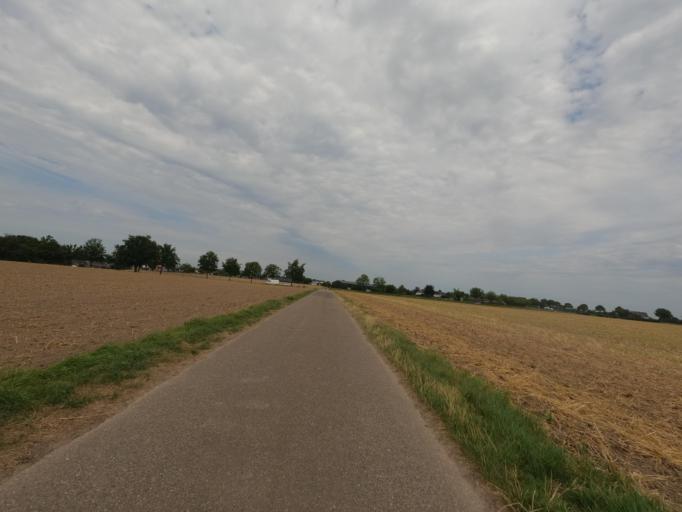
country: DE
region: North Rhine-Westphalia
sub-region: Regierungsbezirk Koln
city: Ubach-Palenberg
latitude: 50.9467
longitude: 6.0777
